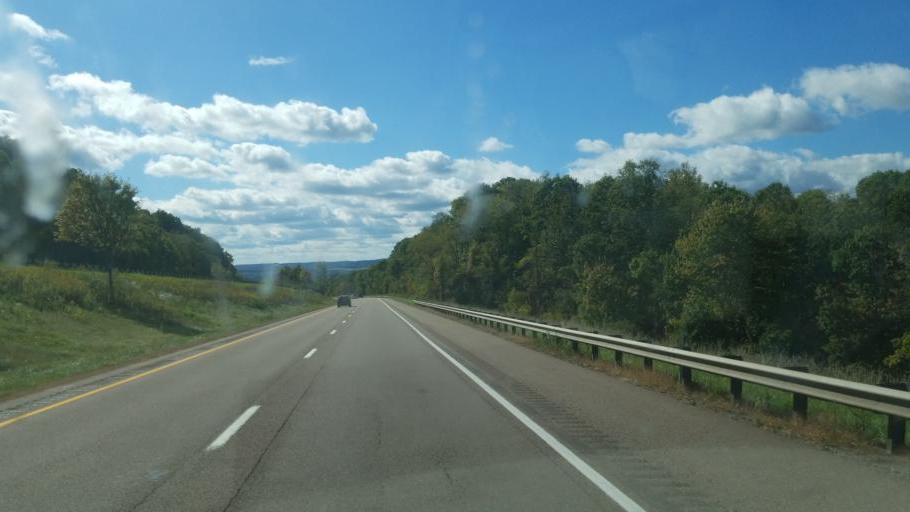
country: US
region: Maryland
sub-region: Garrett County
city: Oakland
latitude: 39.6873
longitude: -79.3534
